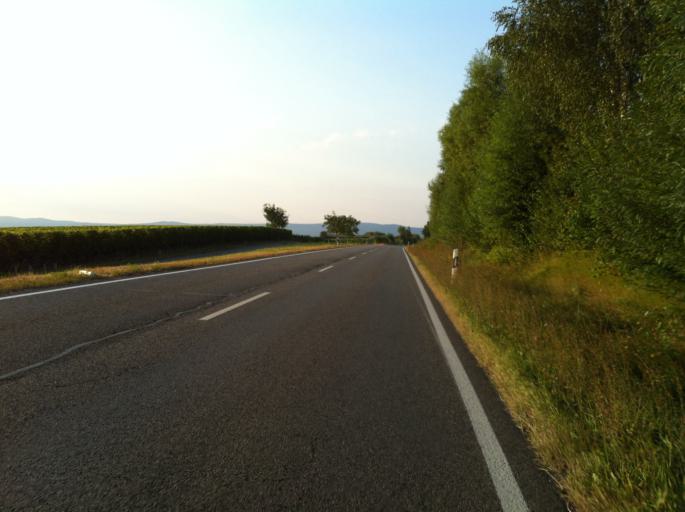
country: DE
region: Rheinland-Pfalz
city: Ingelheim am Rhein
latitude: 49.9486
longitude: 8.0740
